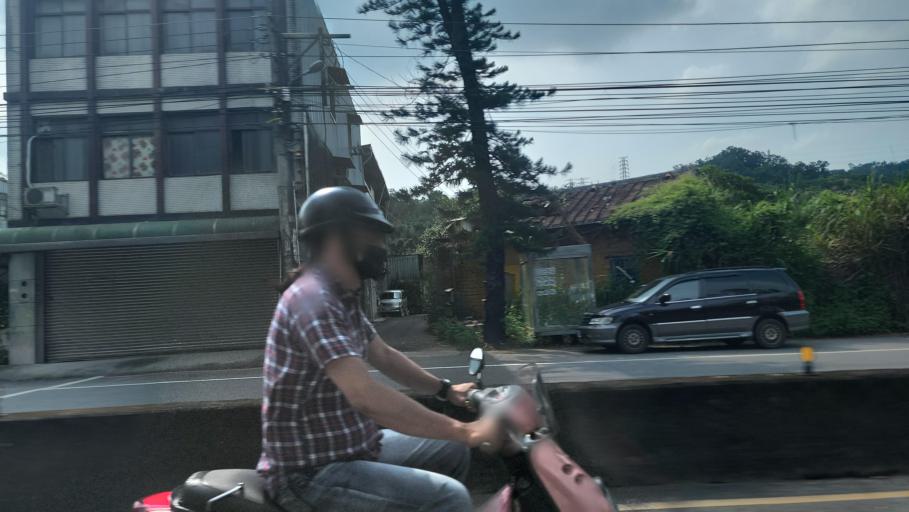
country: TW
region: Taiwan
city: Daxi
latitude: 24.9049
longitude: 121.3576
